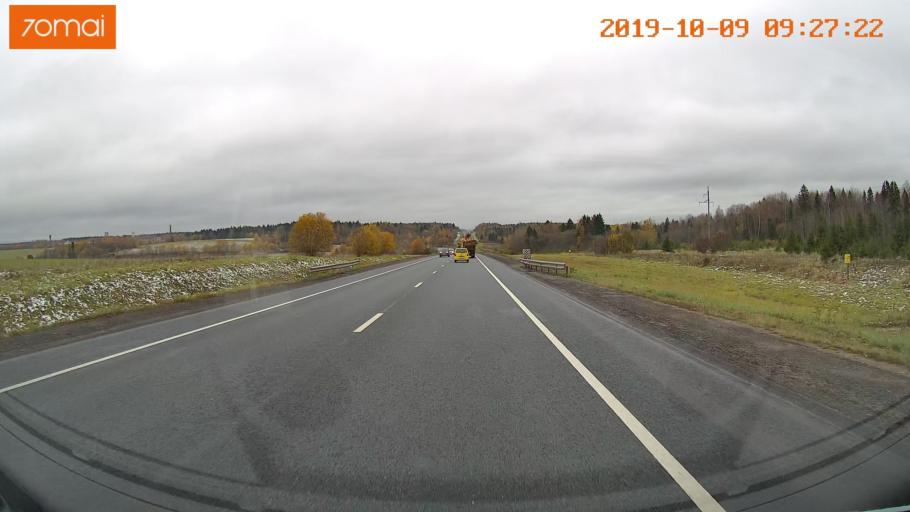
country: RU
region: Vologda
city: Vologda
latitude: 59.1121
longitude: 39.9793
